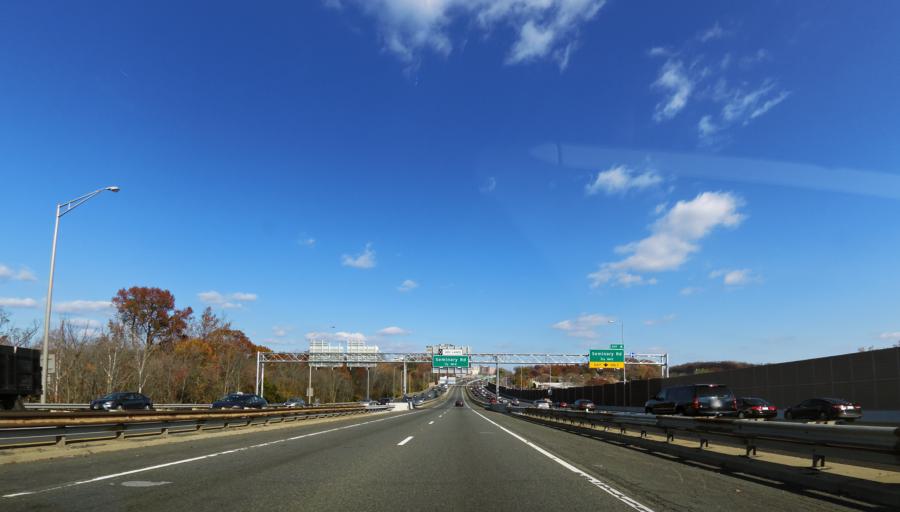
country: US
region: Virginia
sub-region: Fairfax County
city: Lincolnia
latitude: 38.8209
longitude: -77.1284
